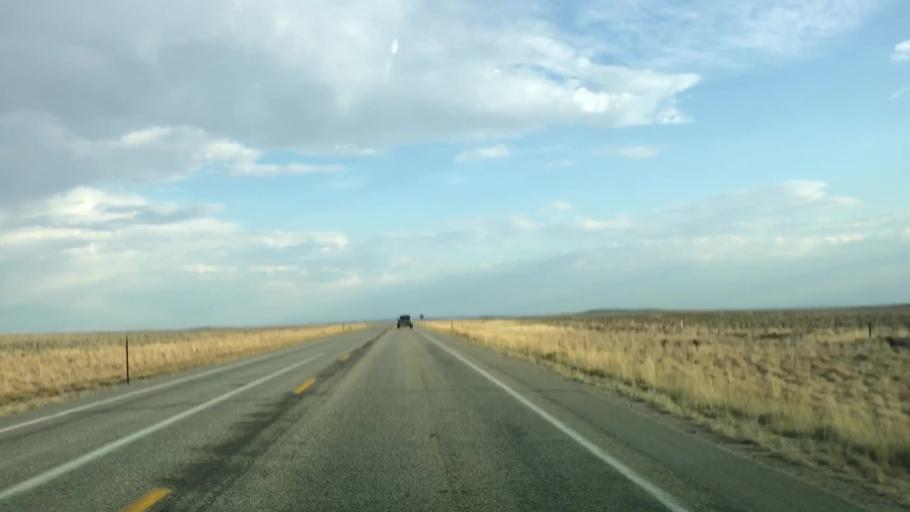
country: US
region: Wyoming
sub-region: Sublette County
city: Pinedale
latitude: 42.3949
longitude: -109.5430
